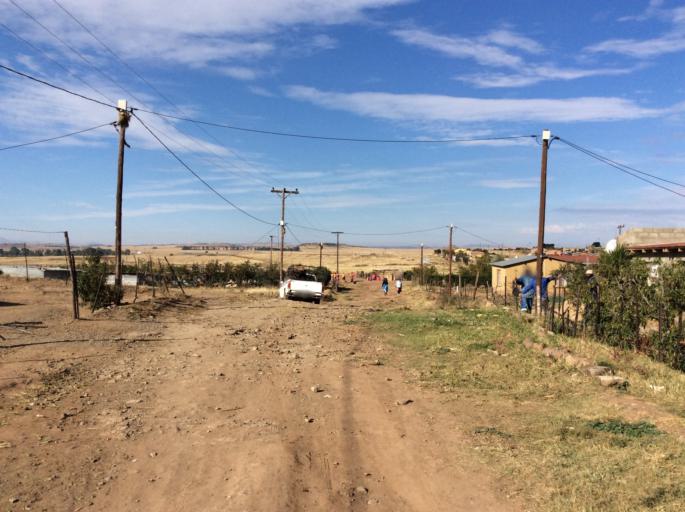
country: LS
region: Mafeteng
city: Mafeteng
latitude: -29.7134
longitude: 27.0152
